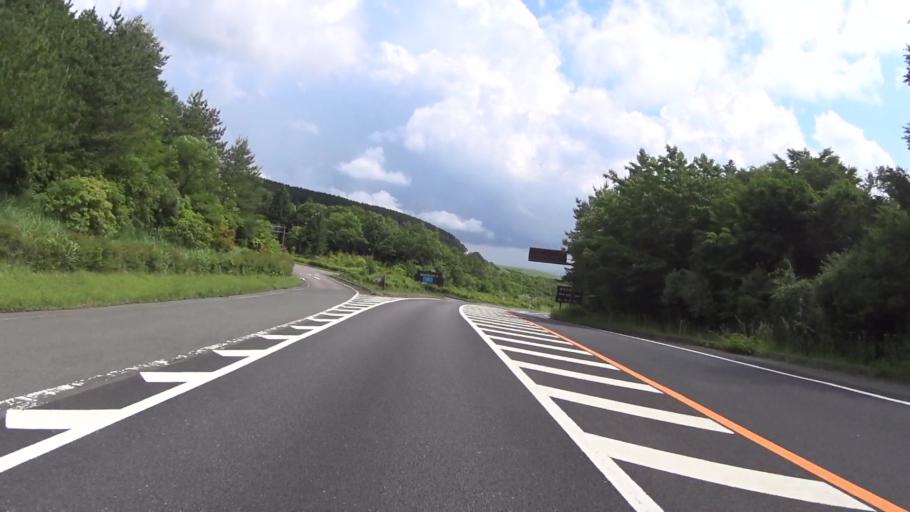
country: JP
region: Kumamoto
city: Aso
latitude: 33.0766
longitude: 131.1958
